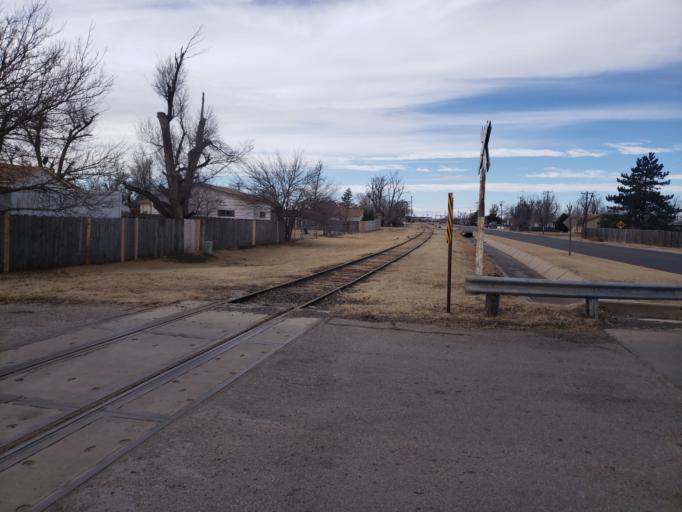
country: US
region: Kansas
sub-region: Ford County
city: Dodge City
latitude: 37.7421
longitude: -100.0148
